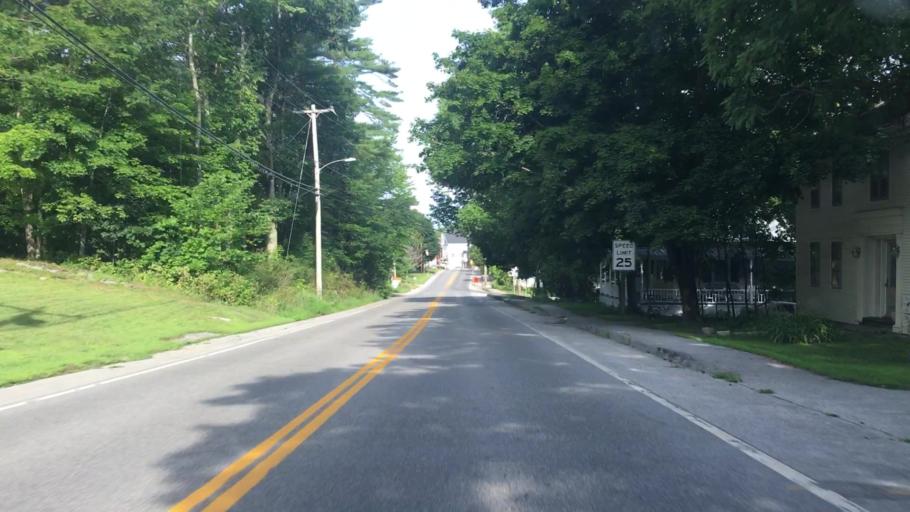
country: US
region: Maine
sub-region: York County
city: Cornish
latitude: 43.8044
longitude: -70.7975
